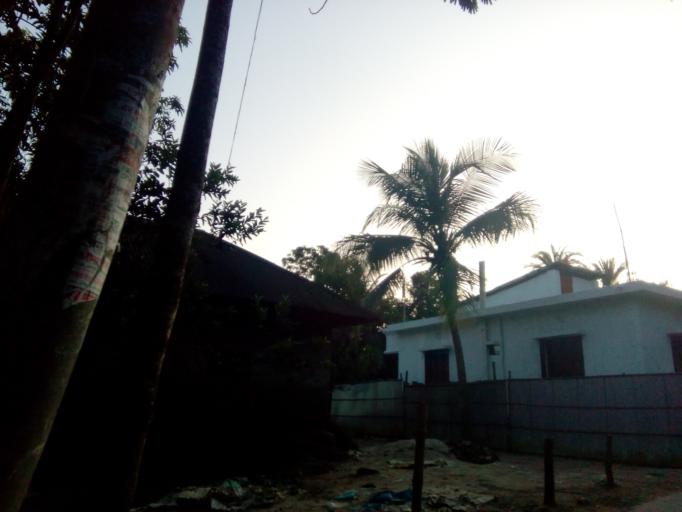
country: BD
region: Chittagong
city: Comilla
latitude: 23.4035
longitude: 91.1919
